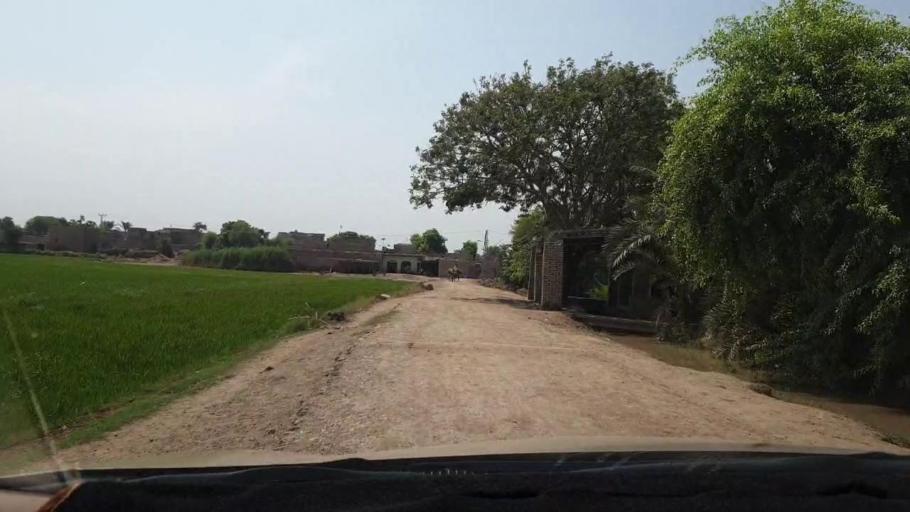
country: PK
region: Sindh
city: Naudero
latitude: 27.6489
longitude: 68.2606
